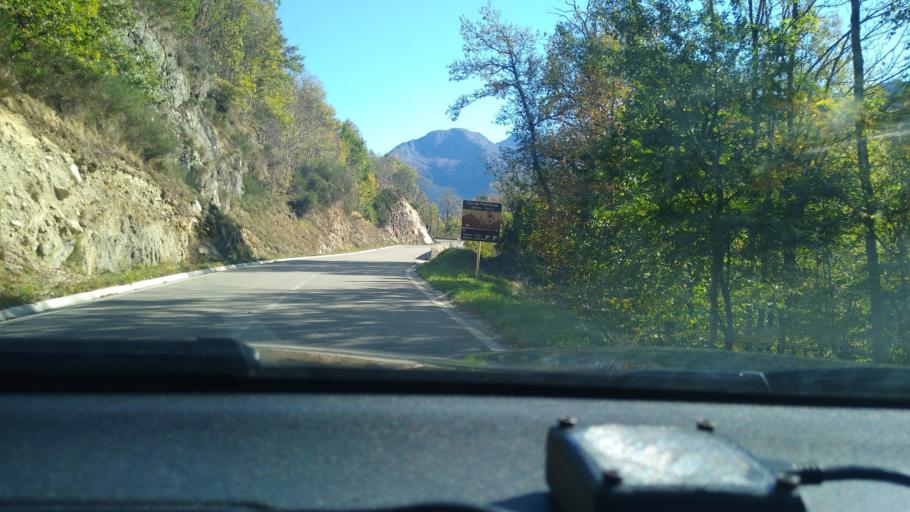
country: FR
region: Midi-Pyrenees
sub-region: Departement de l'Ariege
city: Ax-les-Thermes
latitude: 42.7225
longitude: 1.8583
